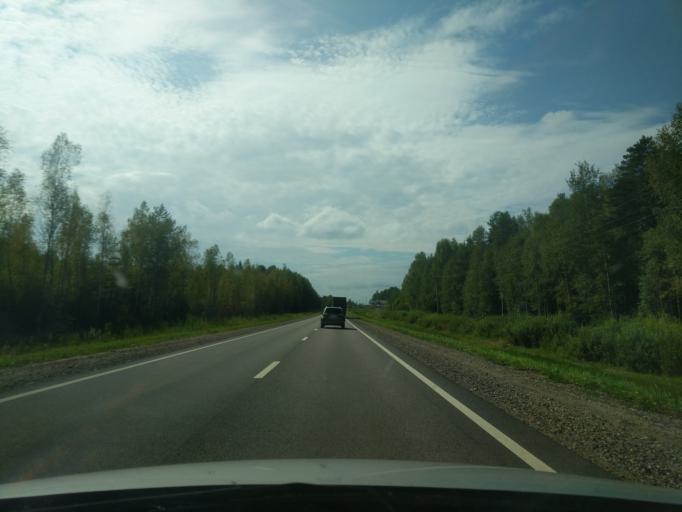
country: RU
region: Kostroma
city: Kadyy
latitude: 57.8027
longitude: 43.2103
